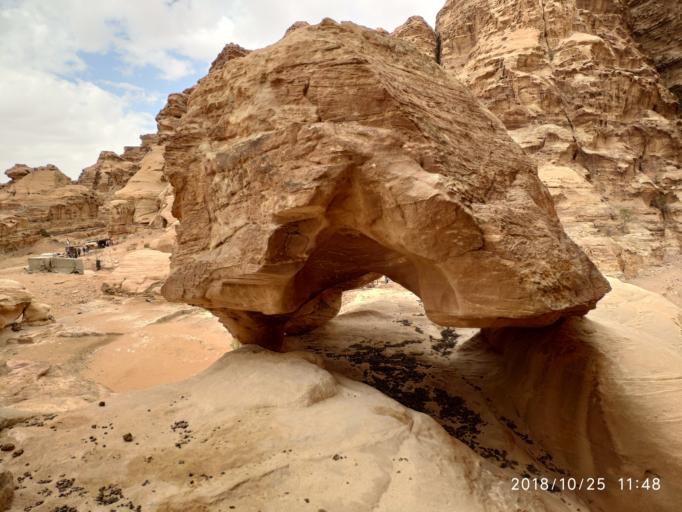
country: JO
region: Ma'an
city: Petra
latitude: 30.3362
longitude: 35.4340
